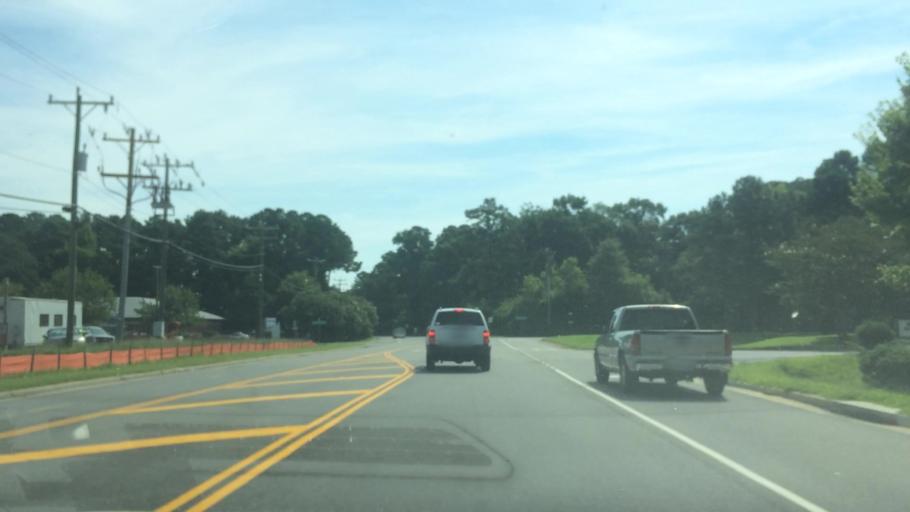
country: US
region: Virginia
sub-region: York County
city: Yorktown
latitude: 37.1606
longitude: -76.4620
